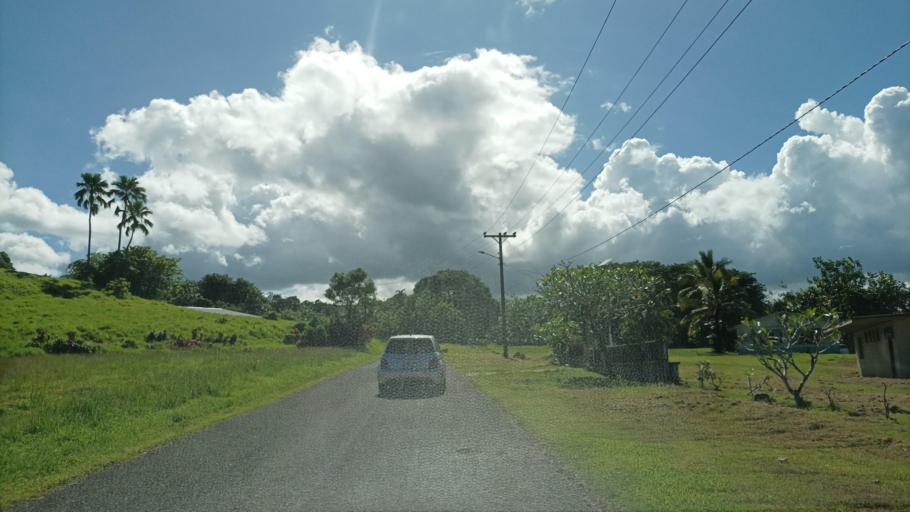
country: FM
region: Pohnpei
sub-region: Madolenihm Municipality
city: Madolenihm Municipality Government
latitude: 6.8426
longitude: 158.3084
